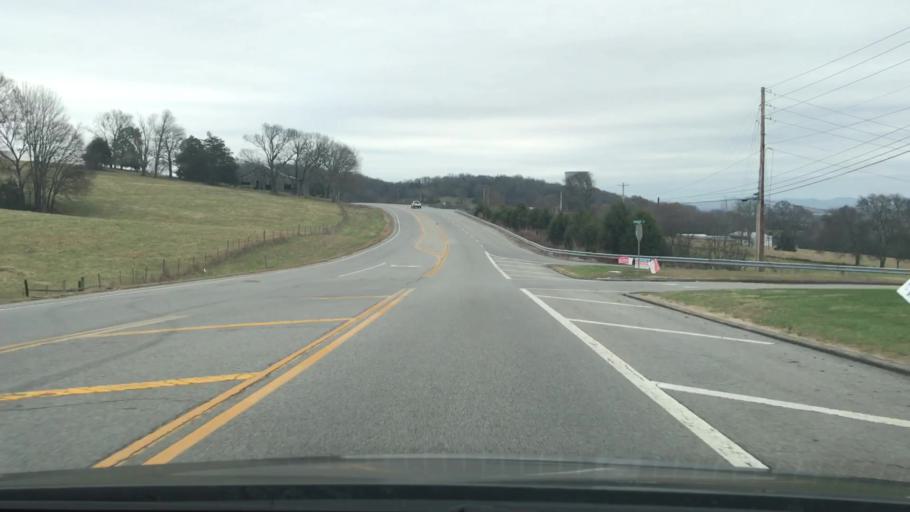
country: US
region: Tennessee
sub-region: Trousdale County
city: Hartsville
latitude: 36.3736
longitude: -86.1087
